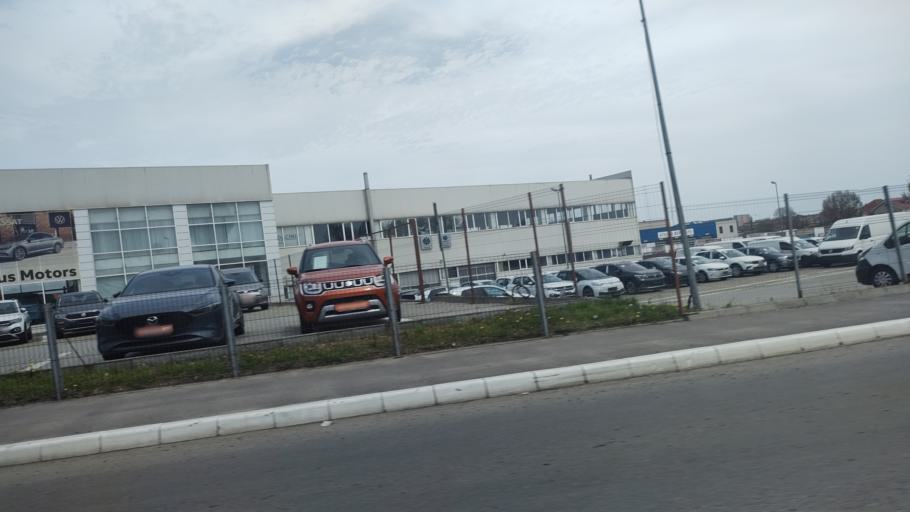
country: RO
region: Constanta
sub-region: Municipiul Constanta
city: Constanta
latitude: 44.1730
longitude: 28.5950
